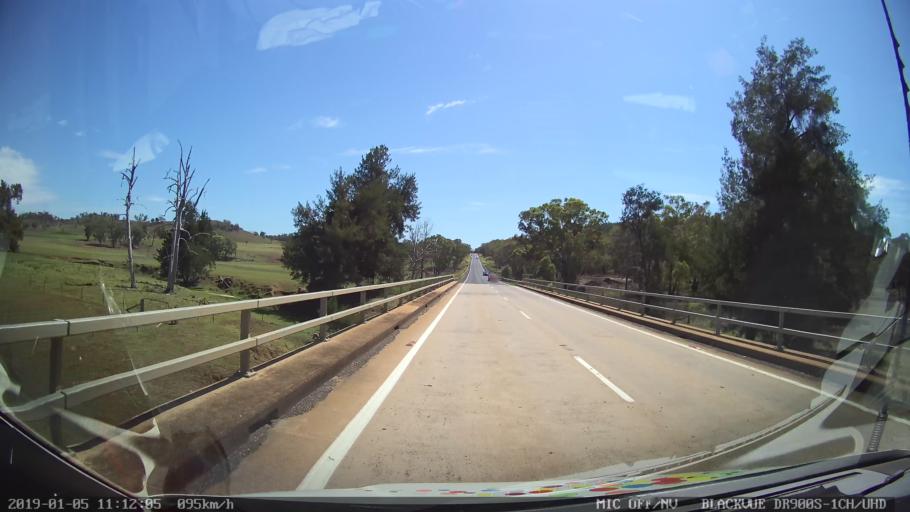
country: AU
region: New South Wales
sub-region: Warrumbungle Shire
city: Coonabarabran
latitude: -31.3857
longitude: 149.2567
